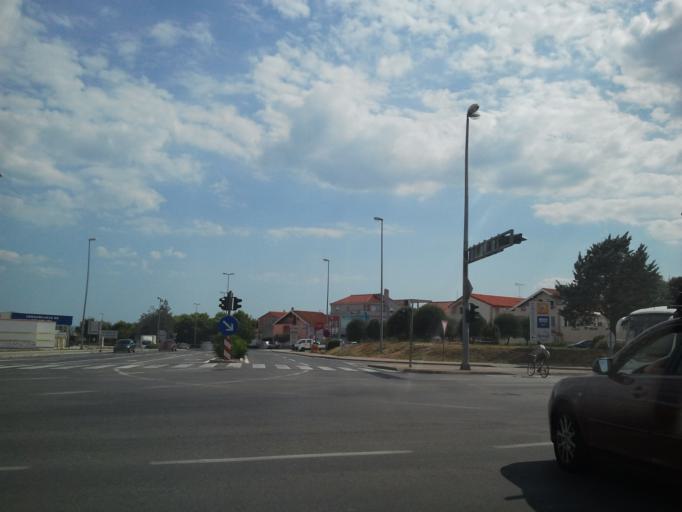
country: HR
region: Zadarska
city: Zadar
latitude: 44.1143
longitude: 15.2540
